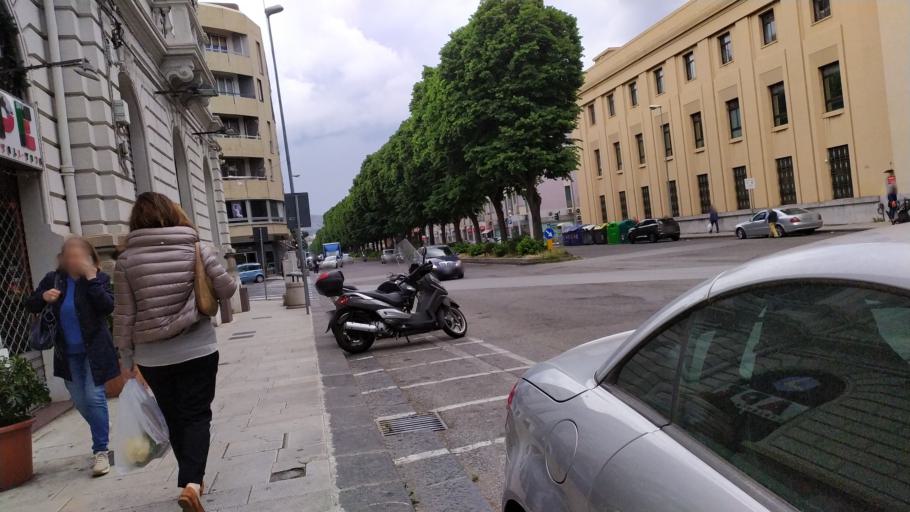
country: IT
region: Sicily
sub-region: Messina
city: Messina
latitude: 38.1897
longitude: 15.5563
